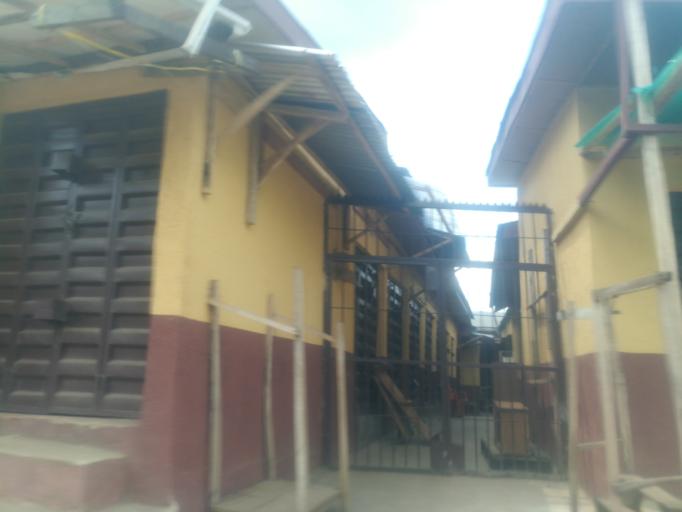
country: NG
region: Oyo
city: Ibadan
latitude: 7.3885
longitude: 3.8864
